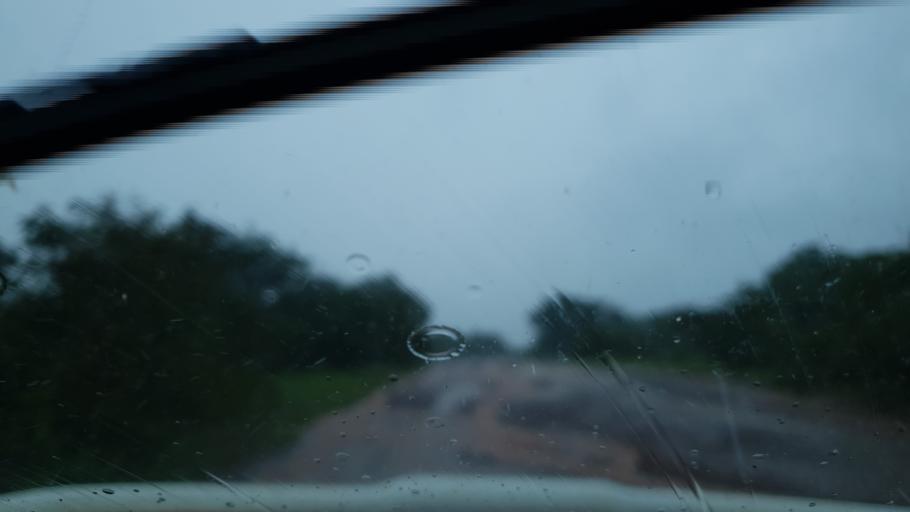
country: ML
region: Sikasso
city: Kolondieba
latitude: 11.6188
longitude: -6.6791
